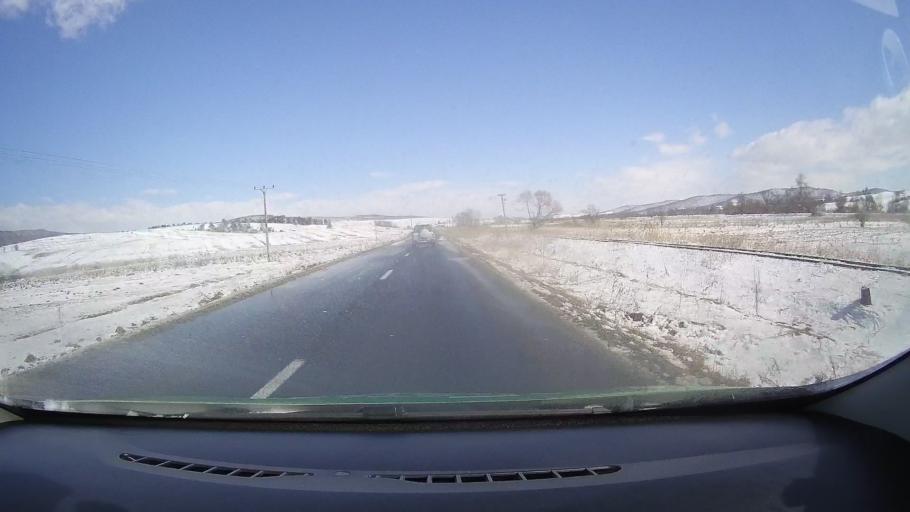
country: RO
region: Sibiu
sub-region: Comuna Rosia
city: Rosia
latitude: 45.8068
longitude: 24.3566
